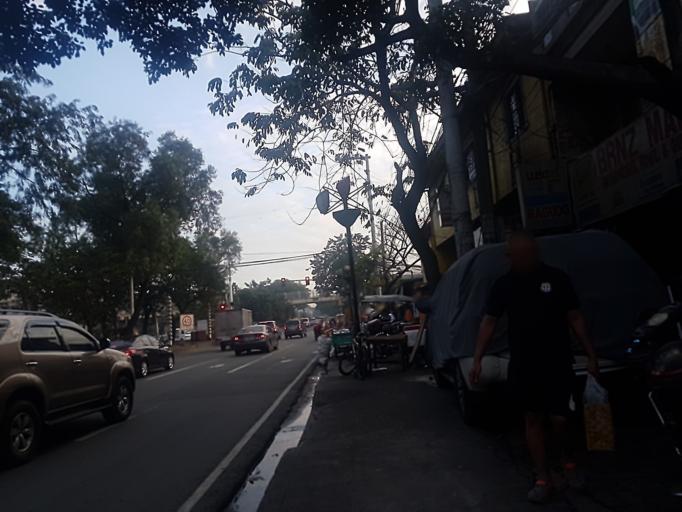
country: PH
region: Metro Manila
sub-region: City of Manila
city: Quiapo
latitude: 14.5868
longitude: 121.0018
